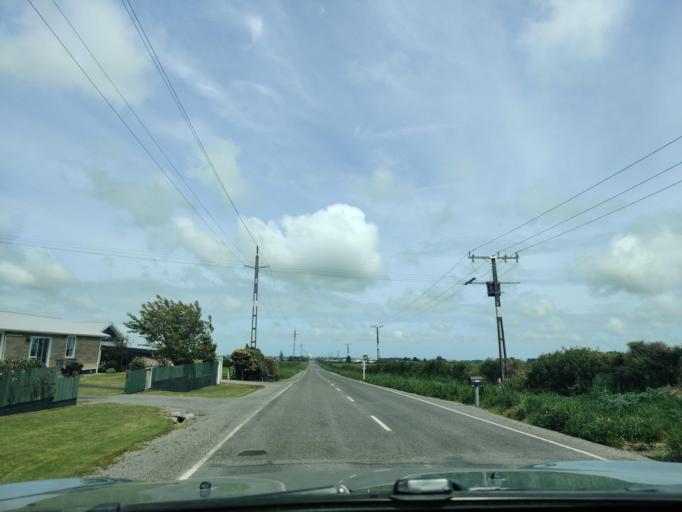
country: NZ
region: Taranaki
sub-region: South Taranaki District
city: Eltham
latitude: -39.4285
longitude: 174.1697
